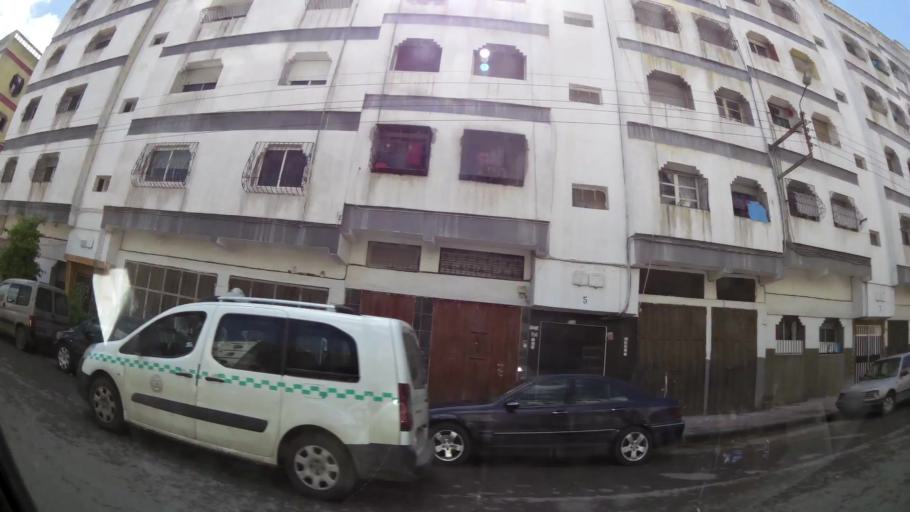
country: MA
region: Grand Casablanca
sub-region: Mediouna
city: Tit Mellil
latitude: 33.5365
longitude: -7.5509
